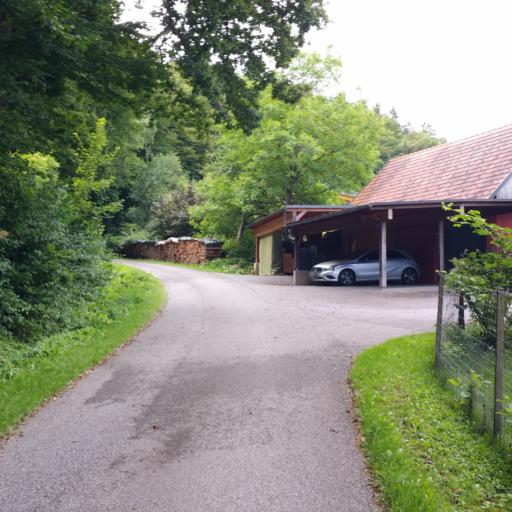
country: AT
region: Styria
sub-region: Politischer Bezirk Leibnitz
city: Gleinstatten
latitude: 46.7449
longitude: 15.3732
